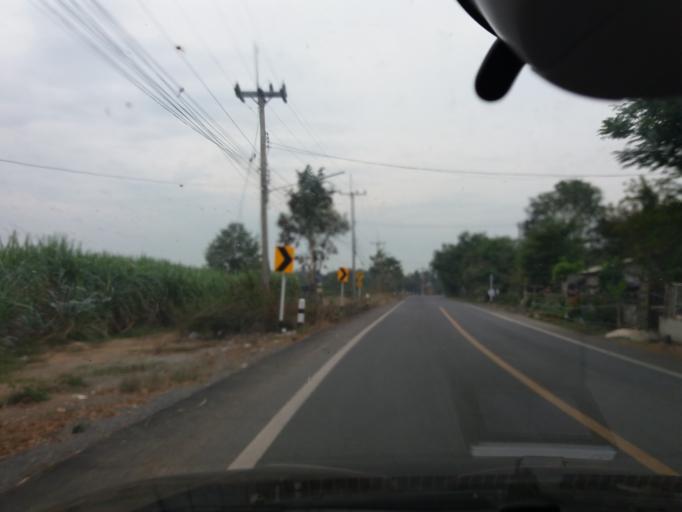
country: TH
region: Suphan Buri
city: Doembang Nangbuat
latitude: 14.8334
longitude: 100.1173
